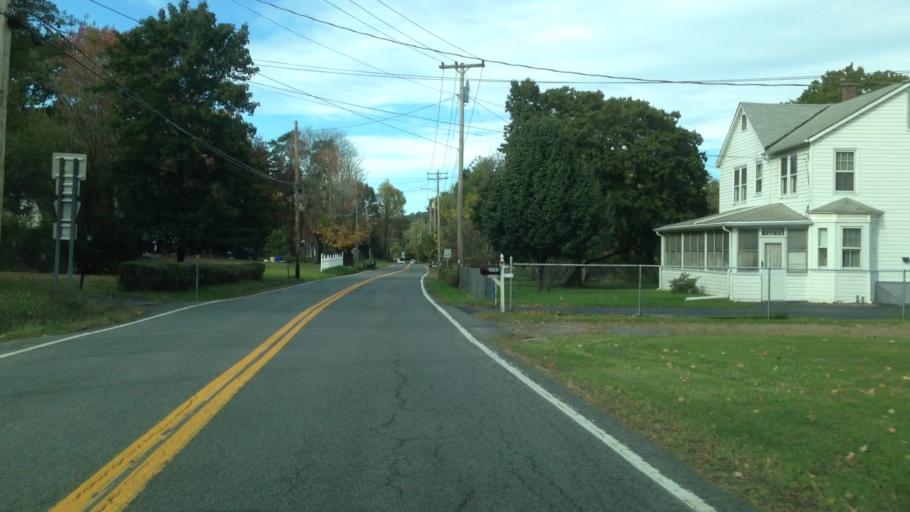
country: US
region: New York
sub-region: Ulster County
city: Tillson
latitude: 41.8400
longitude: -74.0380
